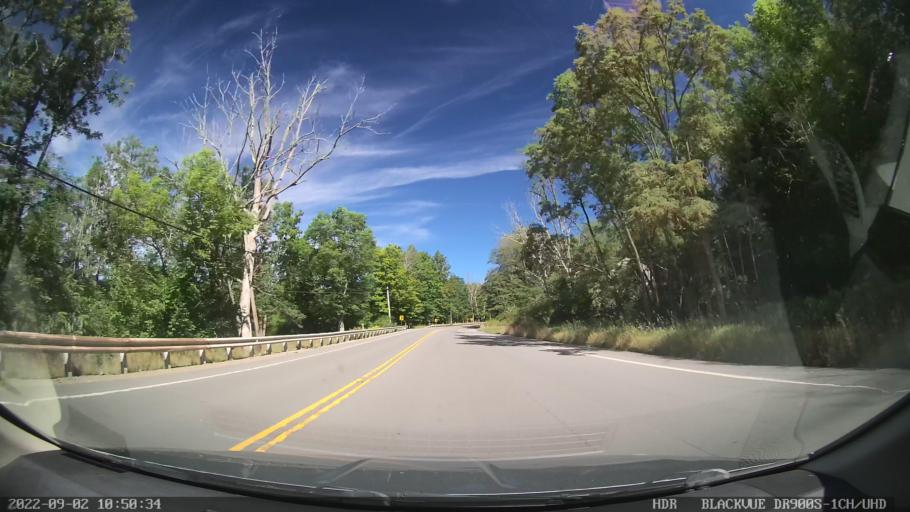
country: US
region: Pennsylvania
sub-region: Tioga County
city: Blossburg
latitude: 41.6156
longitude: -77.1190
